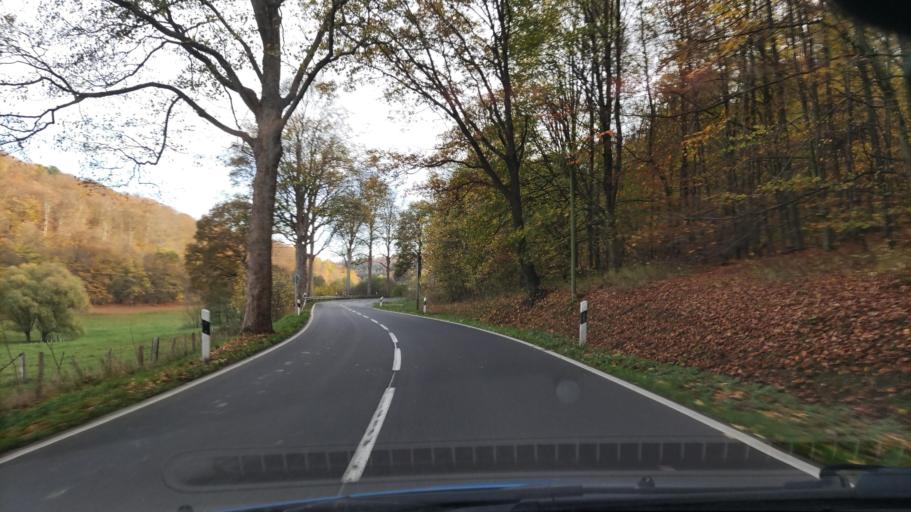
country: DE
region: Lower Saxony
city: Dassel
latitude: 51.7431
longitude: 9.7562
